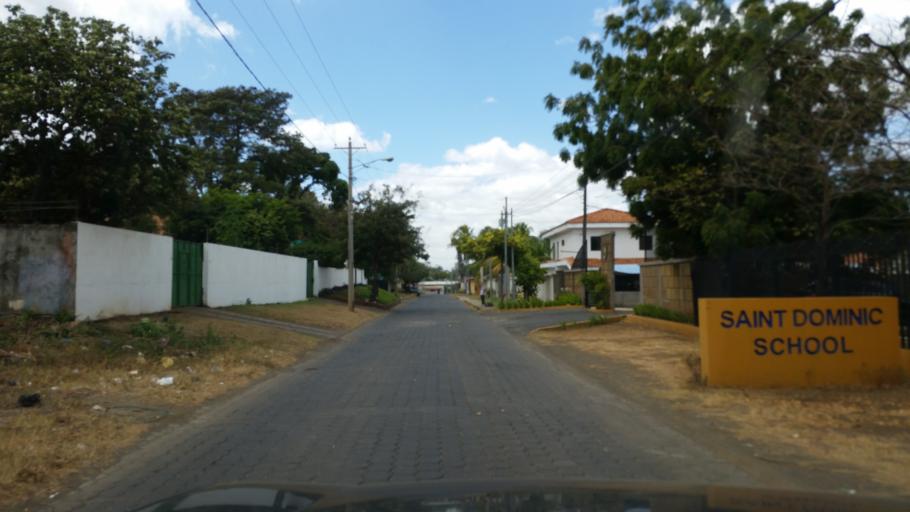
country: NI
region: Managua
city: Managua
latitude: 12.0988
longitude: -86.2296
